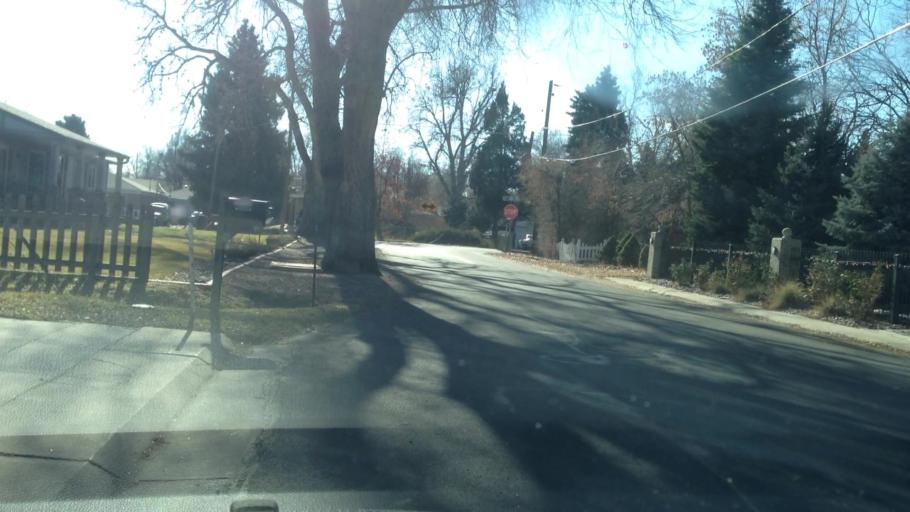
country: US
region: Colorado
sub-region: Jefferson County
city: Lakewood
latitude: 39.7237
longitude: -105.0755
